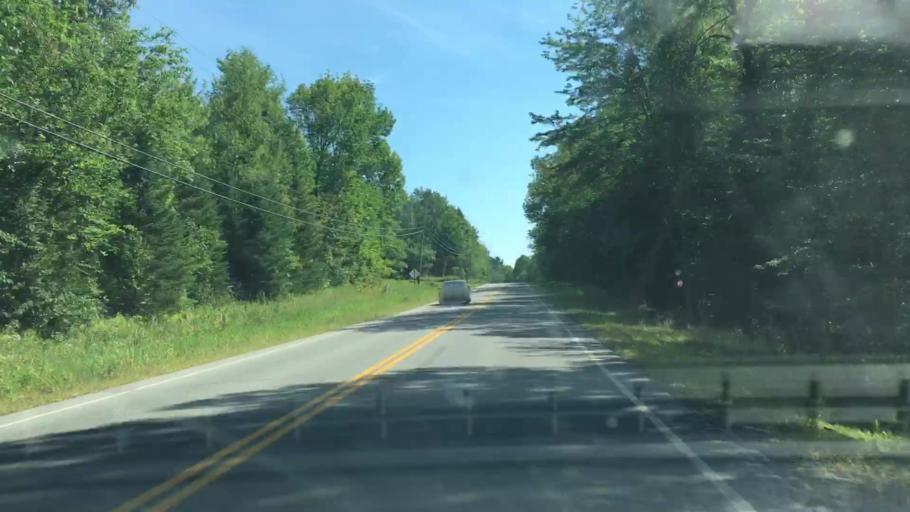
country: US
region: Maine
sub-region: Piscataquis County
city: Milo
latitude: 45.1983
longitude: -68.9050
